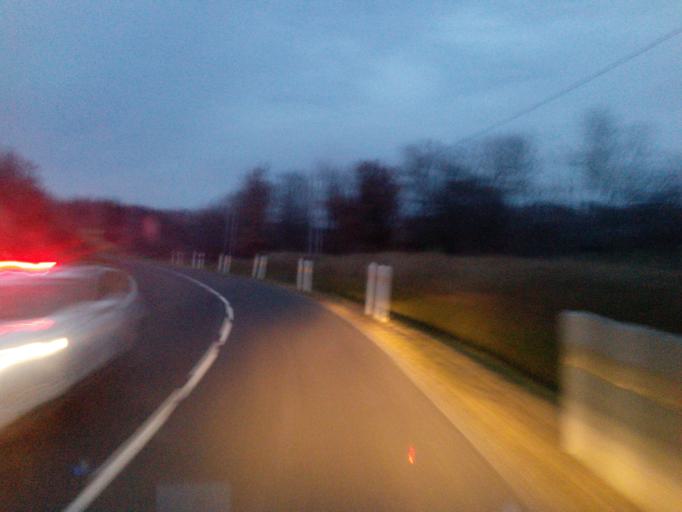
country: FR
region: Languedoc-Roussillon
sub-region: Departement de l'Aude
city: Villeneuve-la-Comptal
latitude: 43.2744
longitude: 1.8265
